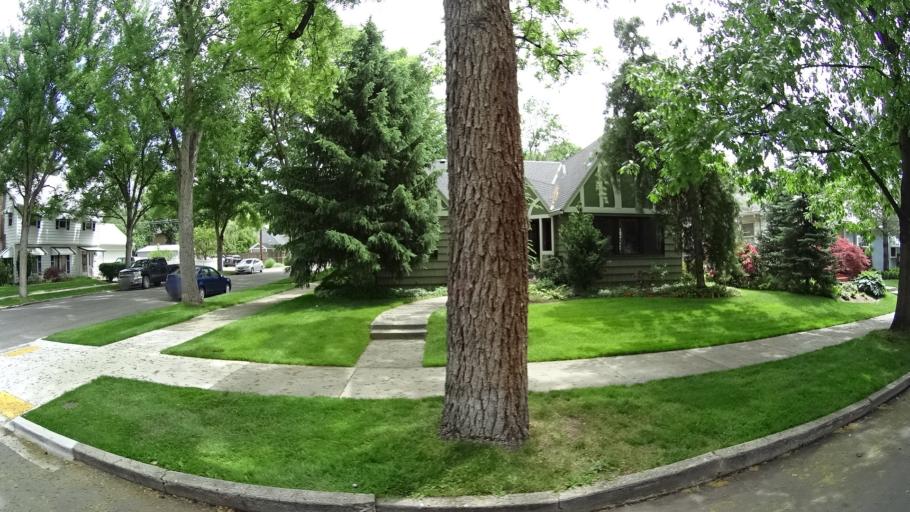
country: US
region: Idaho
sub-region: Ada County
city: Boise
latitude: 43.6310
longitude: -116.2169
